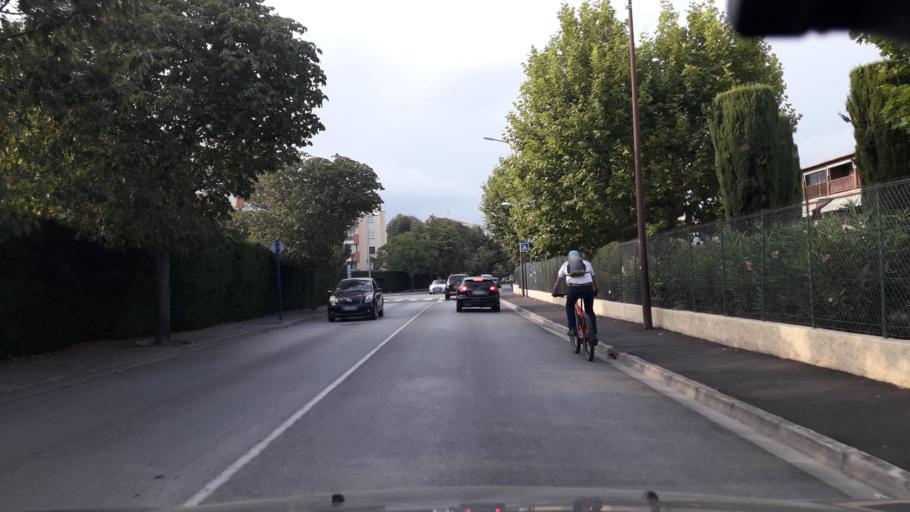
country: FR
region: Provence-Alpes-Cote d'Azur
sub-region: Departement du Var
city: Frejus
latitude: 43.4352
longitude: 6.7540
